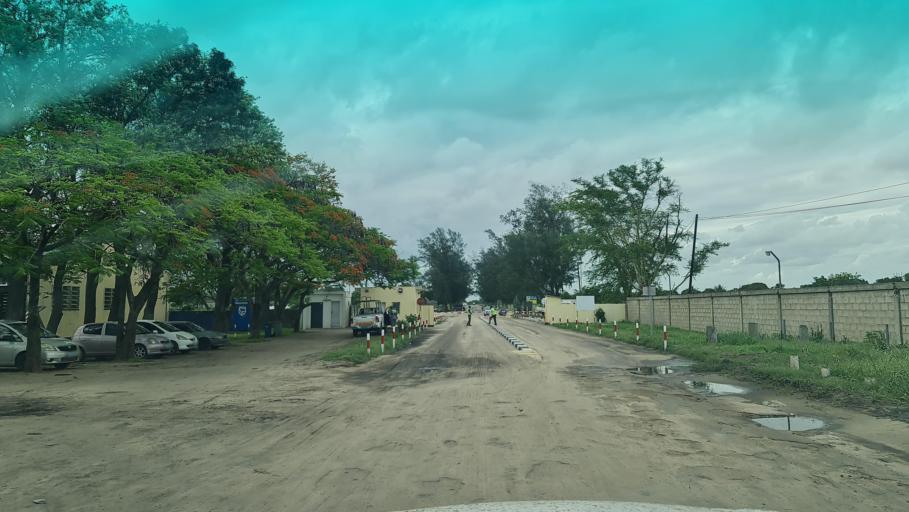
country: MZ
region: Maputo
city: Manhica
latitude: -25.4491
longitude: 32.7772
